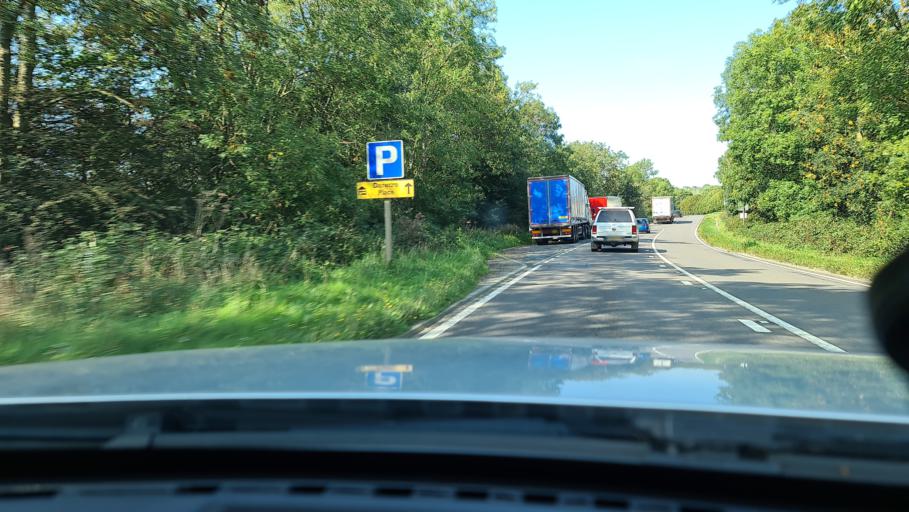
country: GB
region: England
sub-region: Northamptonshire
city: Daventry
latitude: 52.2437
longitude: -1.1390
